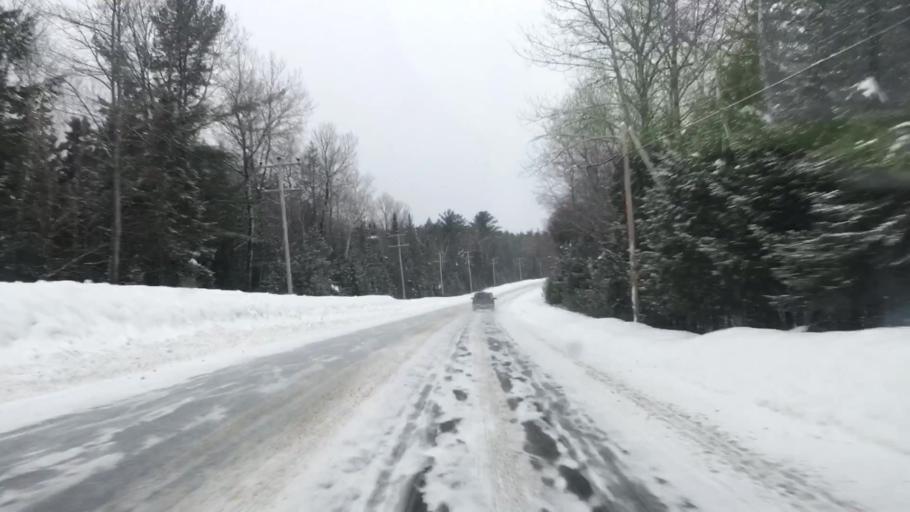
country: US
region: Maine
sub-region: Penobscot County
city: Medway
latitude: 45.5960
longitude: -68.4787
